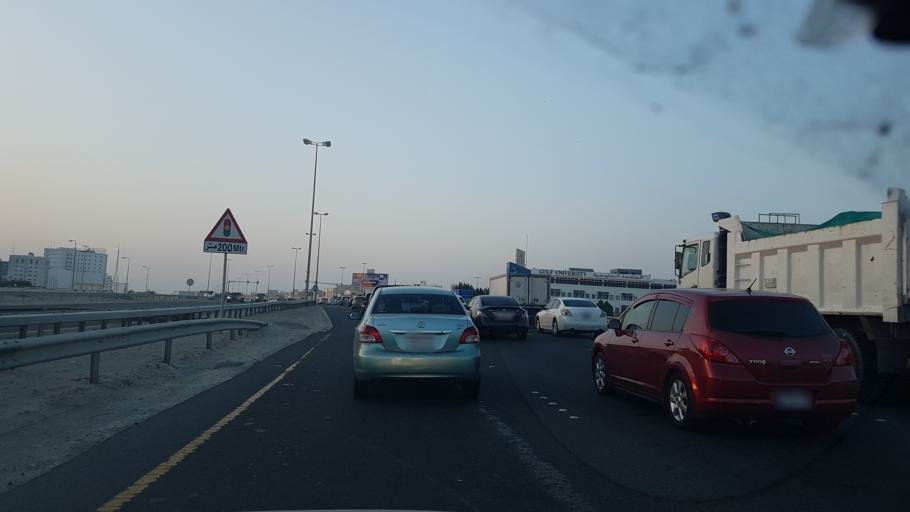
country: BH
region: Northern
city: Ar Rifa'
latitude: 26.1494
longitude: 50.5757
